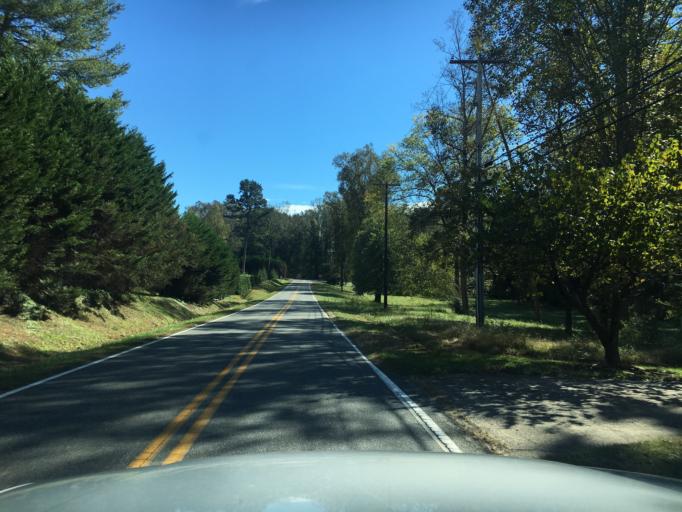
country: US
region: North Carolina
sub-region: Burke County
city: Salem
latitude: 35.7239
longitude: -81.7159
